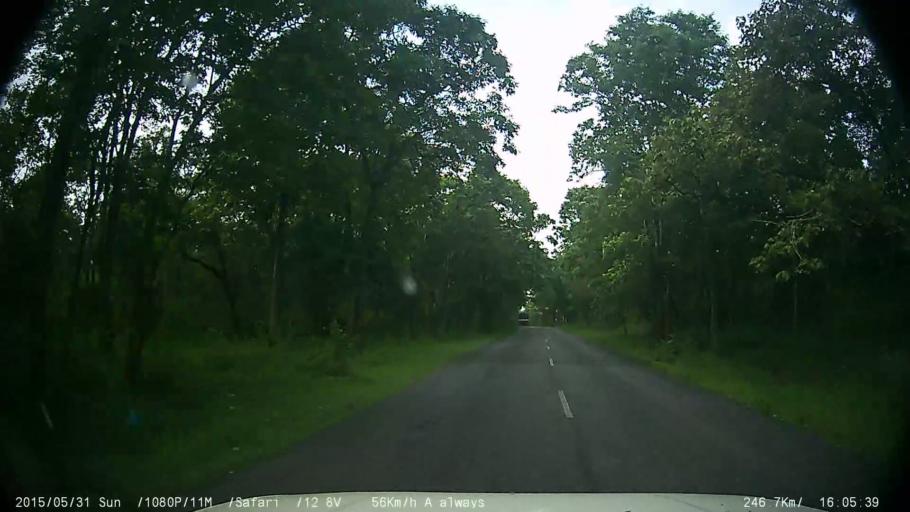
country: IN
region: Tamil Nadu
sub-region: Nilgiri
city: Masinigudi
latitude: 11.7147
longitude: 76.4204
